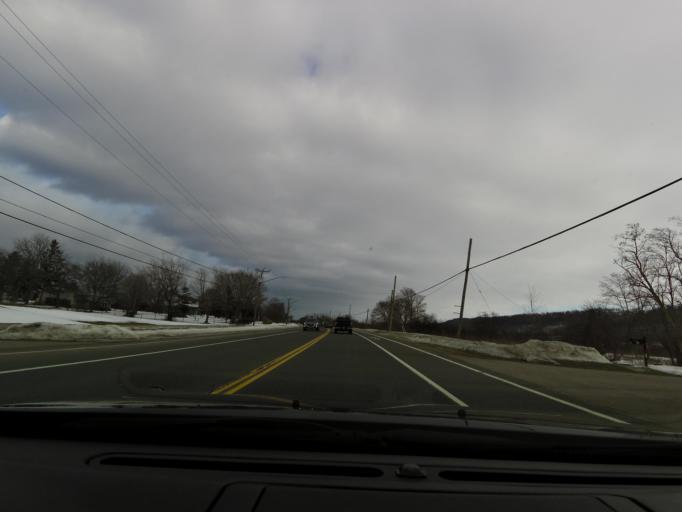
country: CA
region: Ontario
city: Hamilton
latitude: 43.2119
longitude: -79.6972
